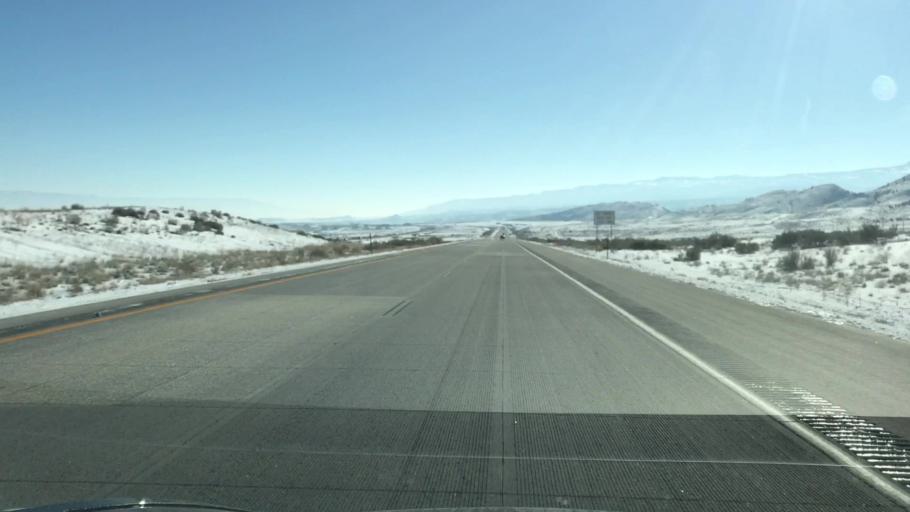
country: US
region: Colorado
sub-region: Mesa County
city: Loma
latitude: 39.1929
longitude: -108.8417
